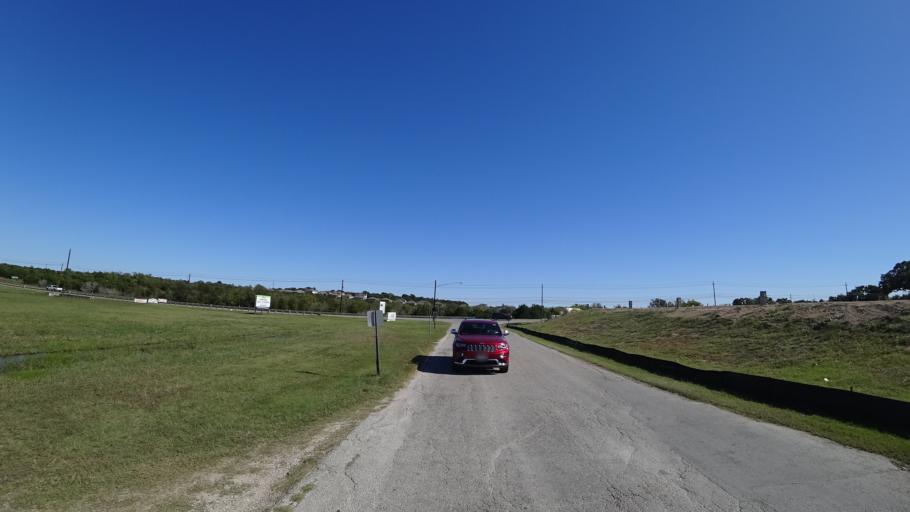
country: US
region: Texas
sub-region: Travis County
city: Hornsby Bend
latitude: 30.2839
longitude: -97.6337
